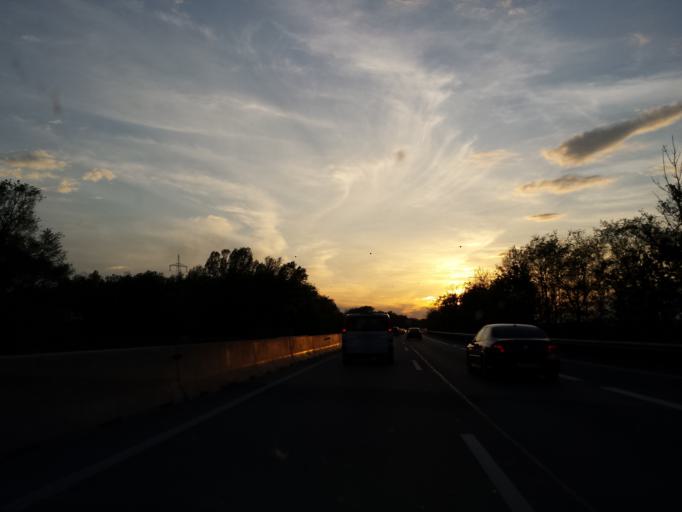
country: AT
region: Lower Austria
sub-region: Politischer Bezirk Bruck an der Leitha
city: Bruck an der Leitha
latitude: 48.0445
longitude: 16.7557
